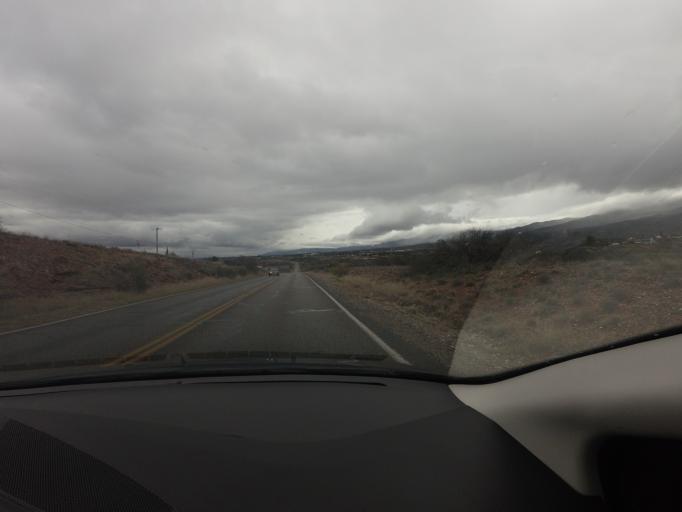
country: US
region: Arizona
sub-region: Yavapai County
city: Clarkdale
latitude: 34.7606
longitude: -112.0390
